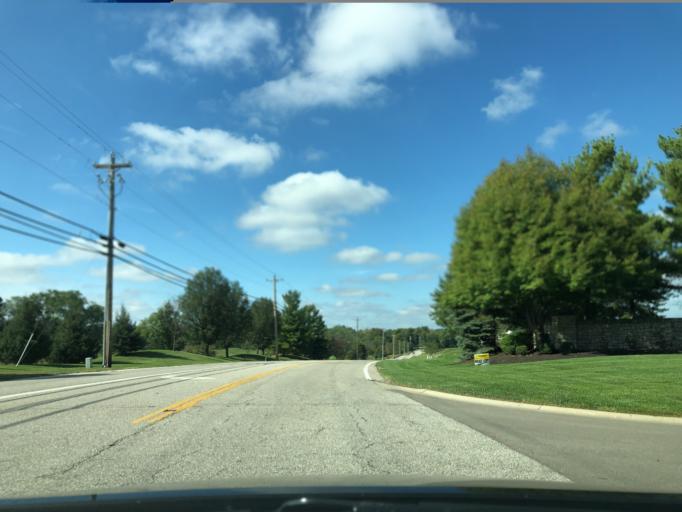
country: US
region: Ohio
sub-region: Hamilton County
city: Loveland
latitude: 39.2395
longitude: -84.2460
